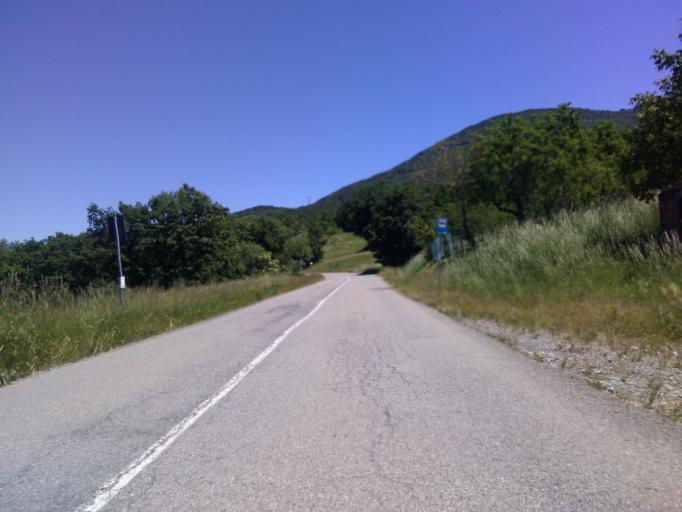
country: IT
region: Emilia-Romagna
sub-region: Provincia di Parma
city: Berceto
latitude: 44.5419
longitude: 10.0325
